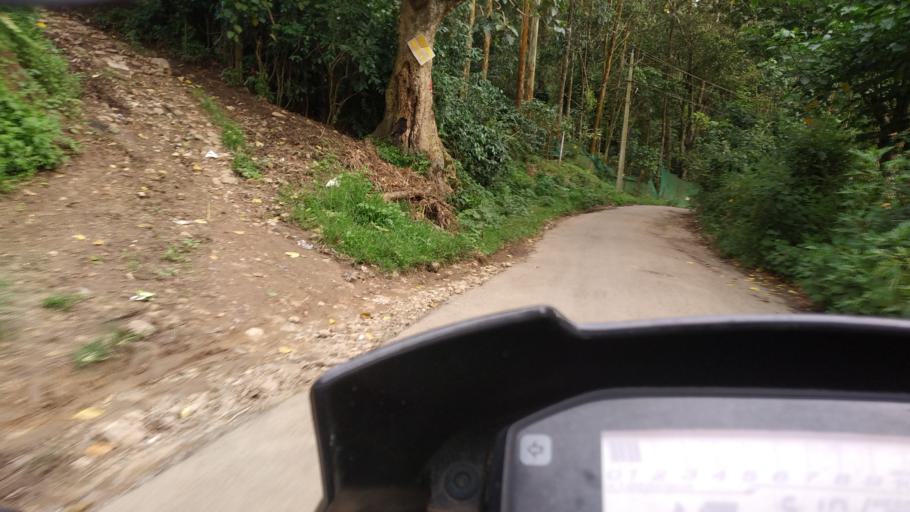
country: IN
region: Tamil Nadu
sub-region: Theni
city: Bodinayakkanur
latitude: 10.0270
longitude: 77.2319
